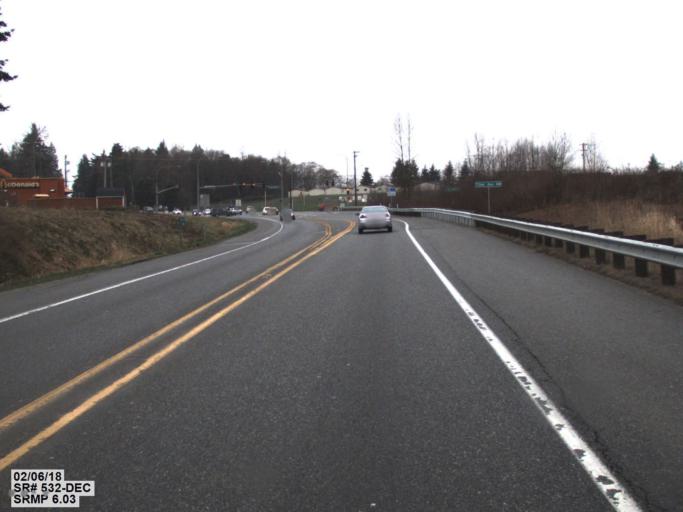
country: US
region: Washington
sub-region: Snohomish County
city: Stanwood
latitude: 48.2391
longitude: -122.3276
